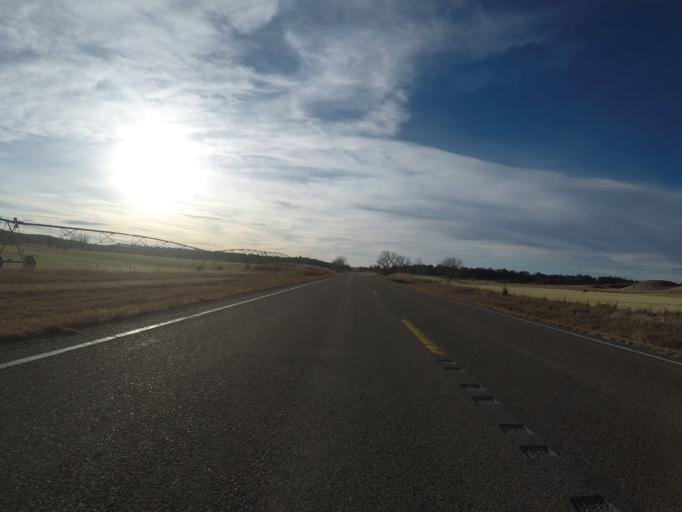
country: US
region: Montana
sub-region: Musselshell County
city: Roundup
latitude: 46.3407
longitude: -108.6901
